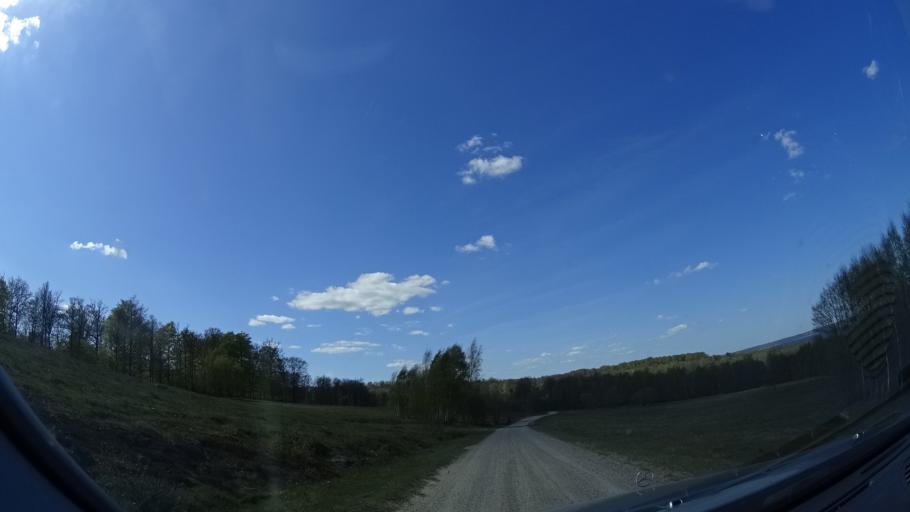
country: SE
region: Skane
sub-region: Hassleholms Kommun
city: Tormestorp
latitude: 56.1038
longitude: 13.7040
